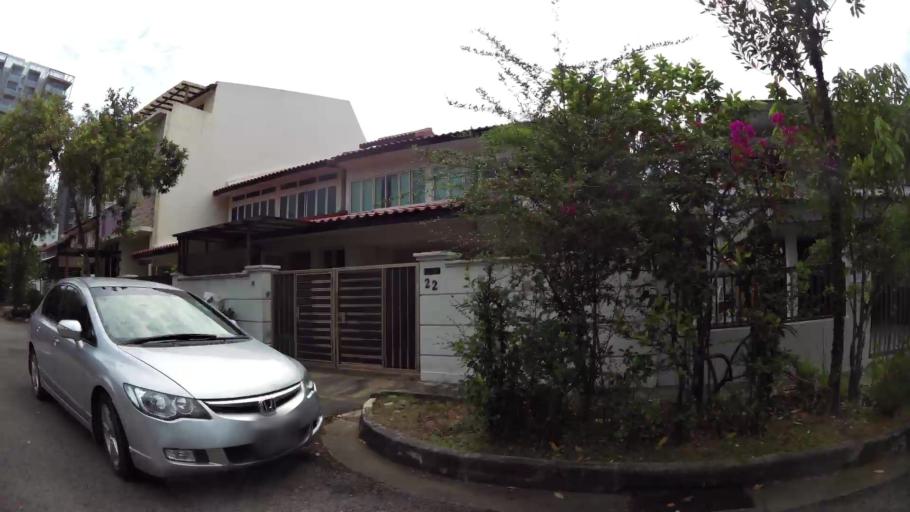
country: SG
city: Singapore
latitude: 1.3153
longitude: 103.7569
